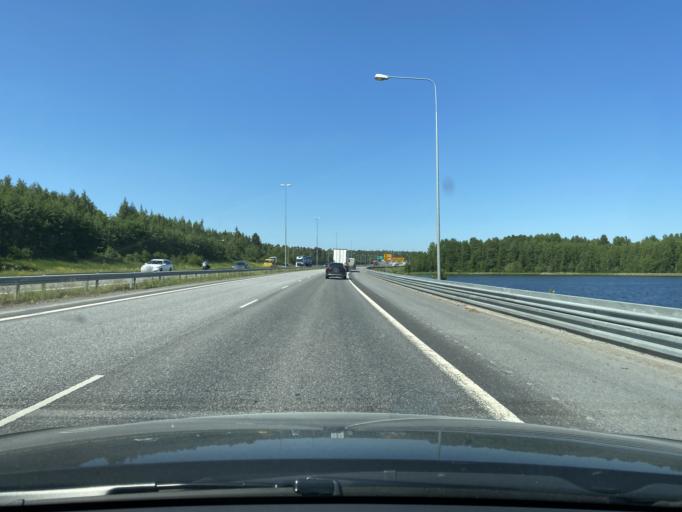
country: FI
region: Pirkanmaa
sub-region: Tampere
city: Pirkkala
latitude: 61.4781
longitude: 23.5882
